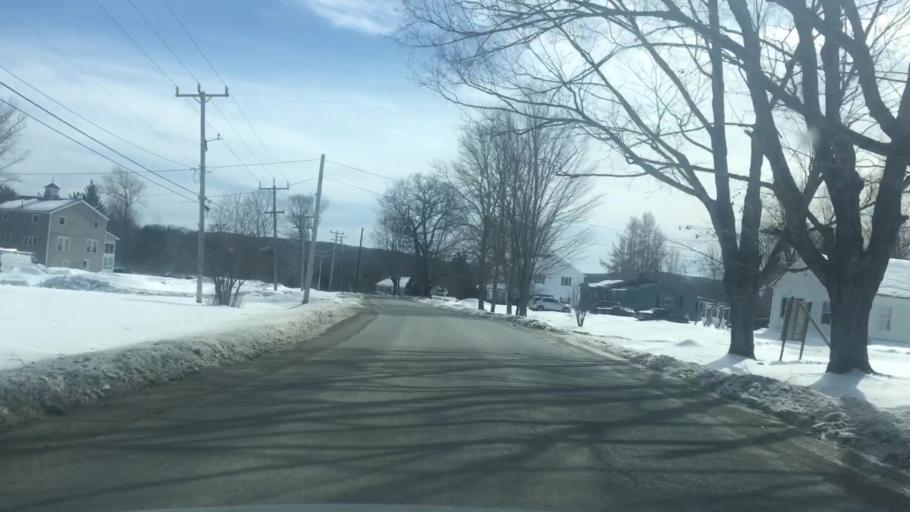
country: US
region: Maine
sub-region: Penobscot County
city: Eddington
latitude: 44.8001
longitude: -68.6794
